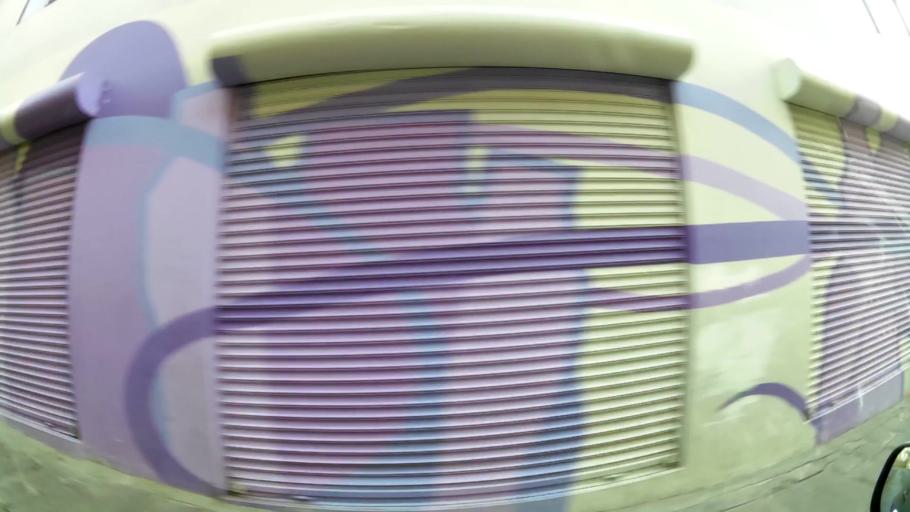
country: BO
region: La Paz
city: La Paz
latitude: -16.4971
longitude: -68.1320
